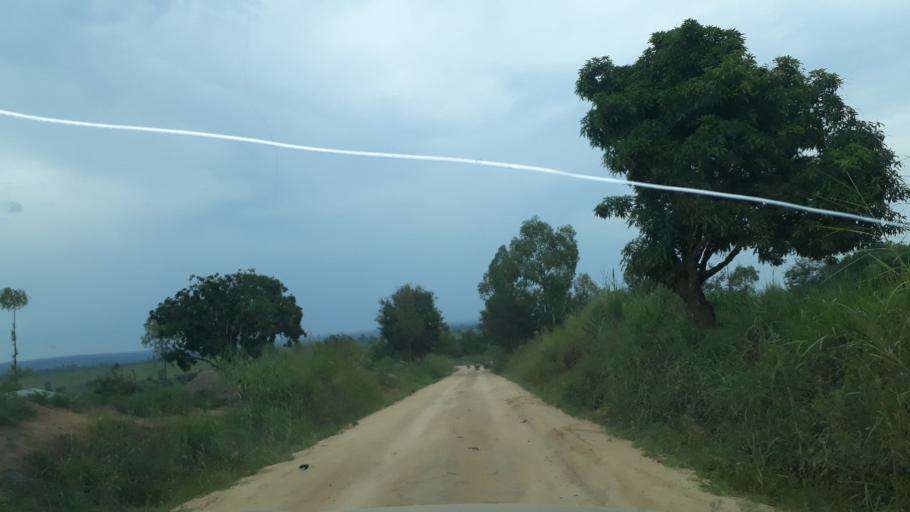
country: CD
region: Eastern Province
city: Bunia
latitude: 1.4688
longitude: 30.1065
